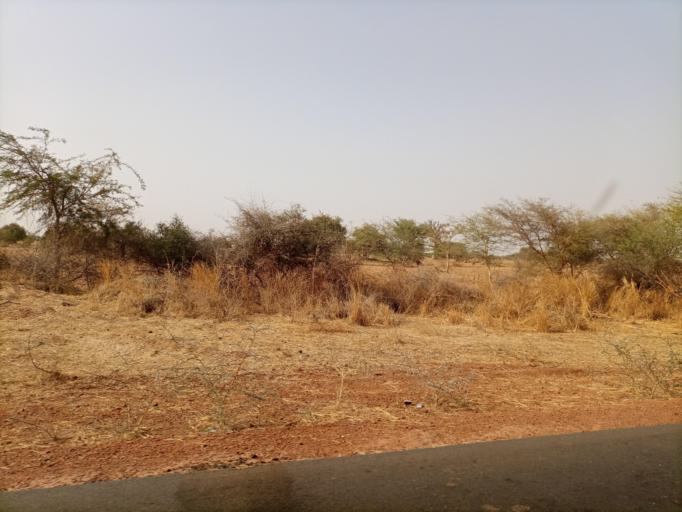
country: SN
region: Fatick
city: Foundiougne
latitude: 14.1269
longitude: -16.4160
